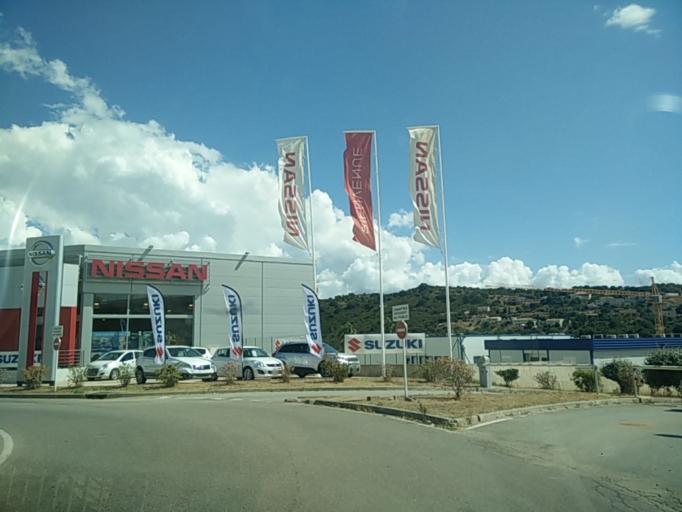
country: FR
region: Corsica
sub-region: Departement de la Corse-du-Sud
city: Afa
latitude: 41.9532
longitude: 8.7984
